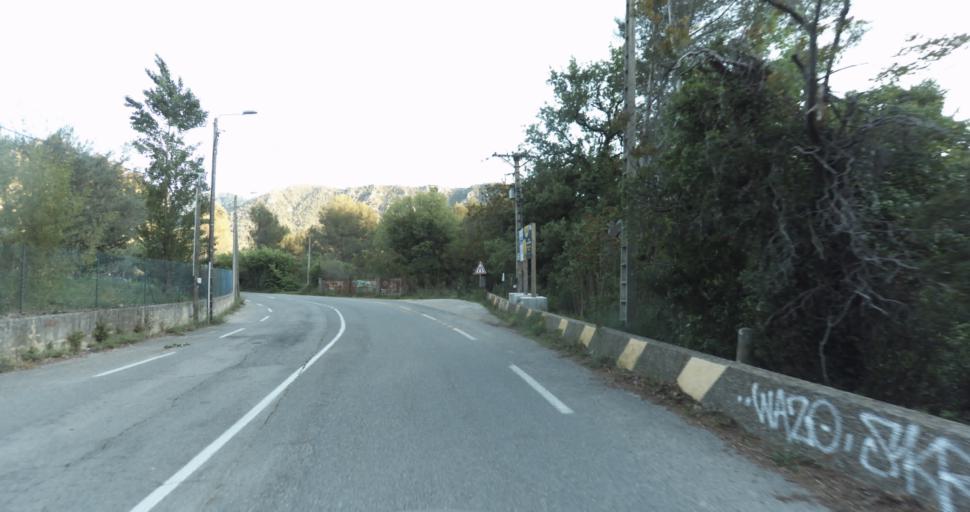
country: FR
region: Provence-Alpes-Cote d'Azur
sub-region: Departement du Var
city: Le Revest-les-Eaux
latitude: 43.1709
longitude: 5.9335
